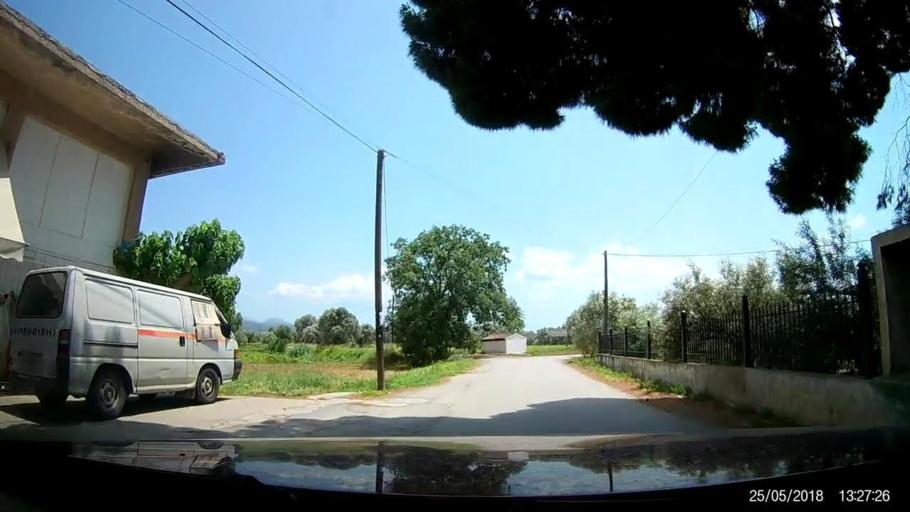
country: GR
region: Central Greece
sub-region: Nomos Evvoias
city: Mytikas
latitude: 38.4506
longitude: 23.6506
